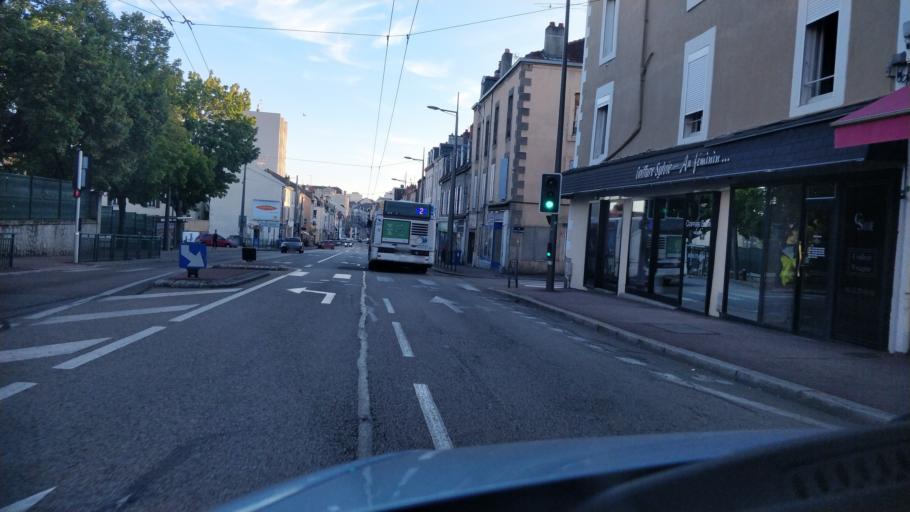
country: FR
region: Limousin
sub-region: Departement de la Haute-Vienne
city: Limoges
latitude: 45.8429
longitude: 1.2591
